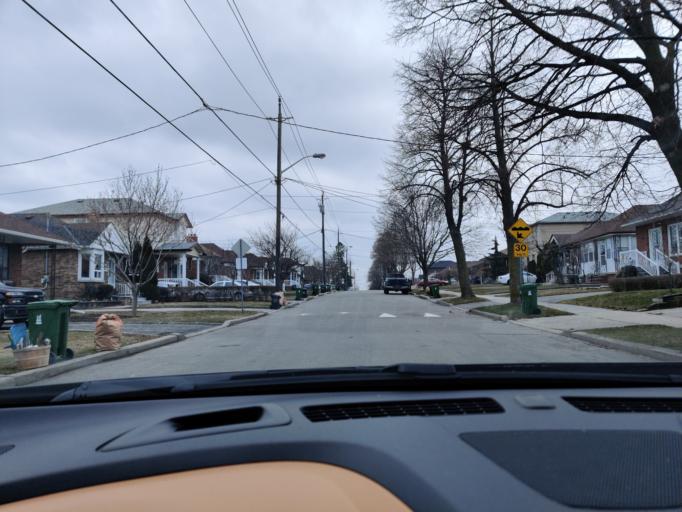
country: CA
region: Ontario
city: Toronto
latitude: 43.7067
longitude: -79.4599
